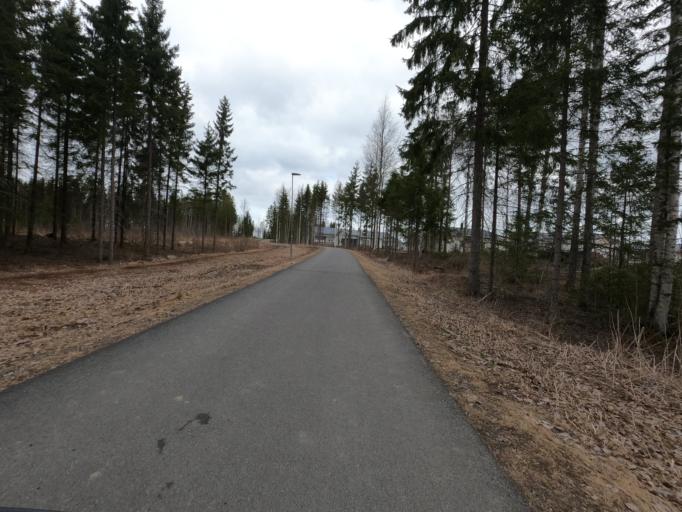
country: FI
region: North Karelia
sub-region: Joensuu
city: Joensuu
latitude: 62.5638
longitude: 29.8211
